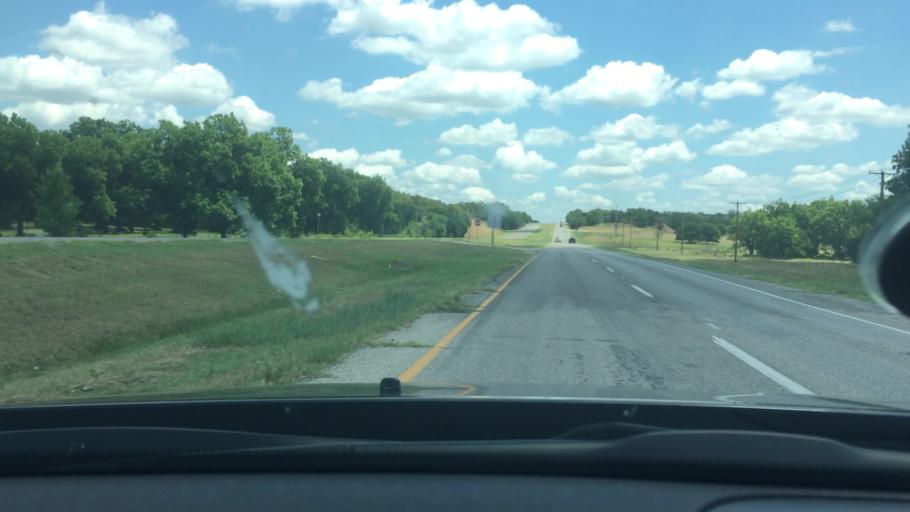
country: US
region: Oklahoma
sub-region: Carter County
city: Wilson
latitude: 34.1729
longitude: -97.3576
